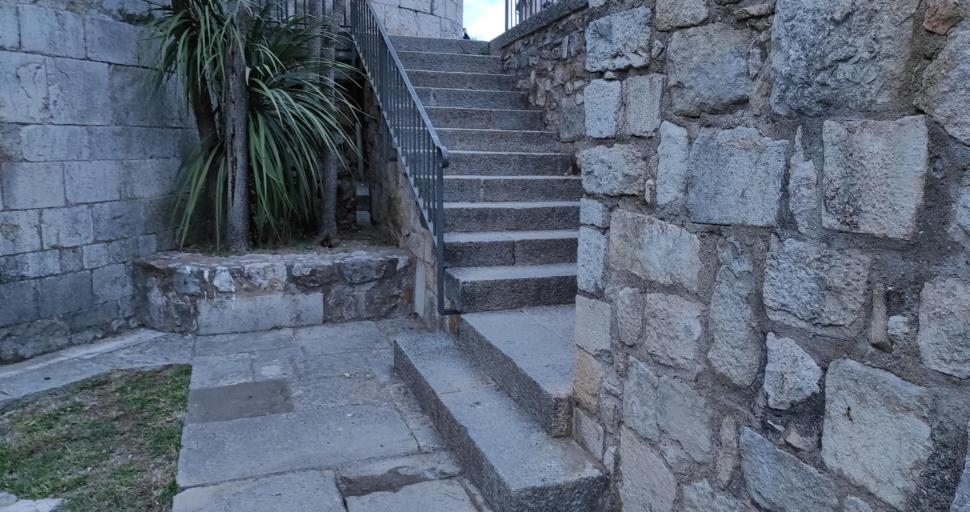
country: ES
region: Catalonia
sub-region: Provincia de Girona
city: Girona
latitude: 41.9887
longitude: 2.8270
